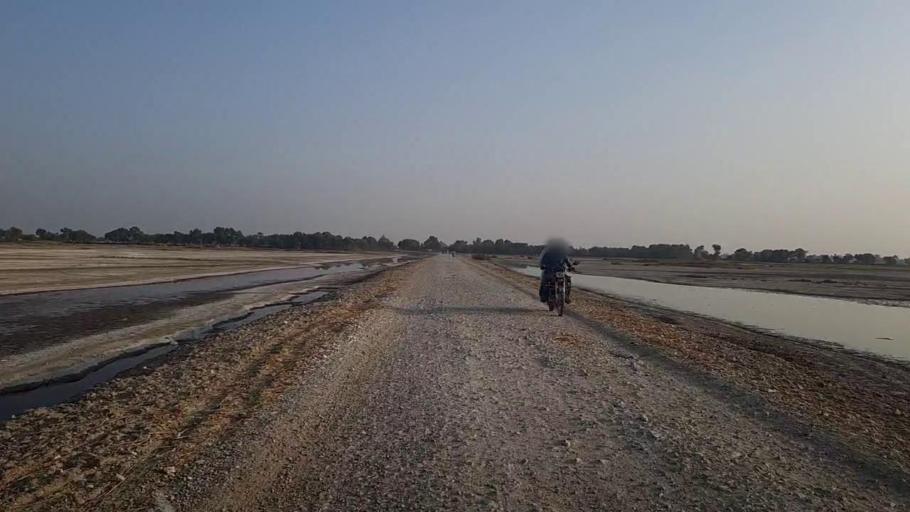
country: PK
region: Sindh
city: Kandhkot
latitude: 28.2458
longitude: 69.0908
